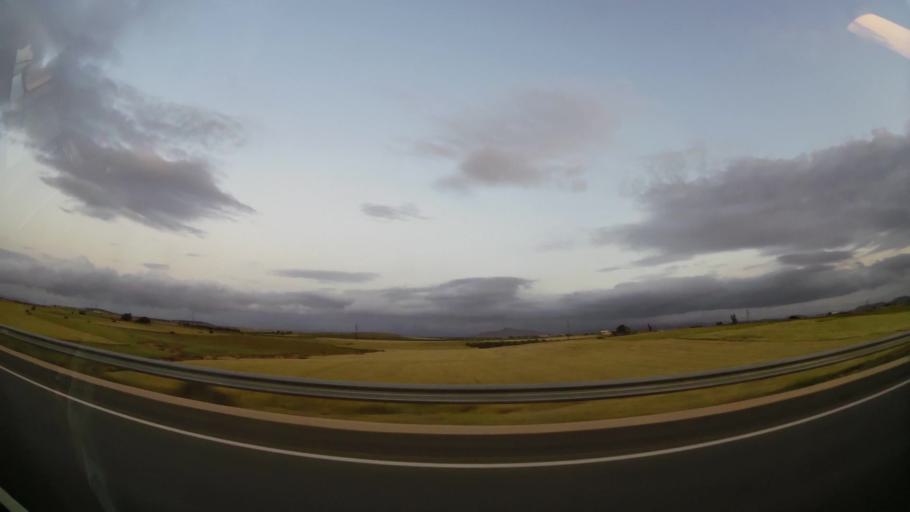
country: MA
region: Oriental
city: El Aioun
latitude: 34.6246
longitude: -2.5378
